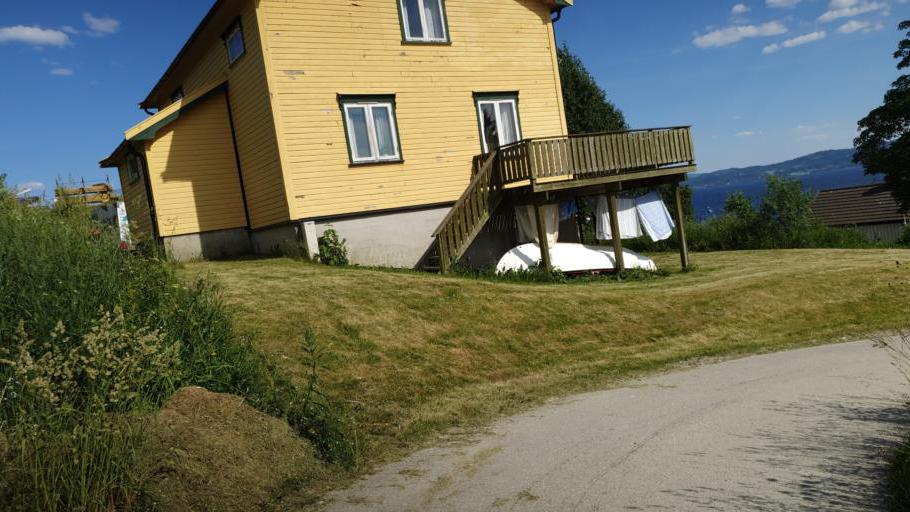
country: NO
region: Nord-Trondelag
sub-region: Leksvik
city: Leksvik
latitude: 63.6722
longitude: 10.6223
